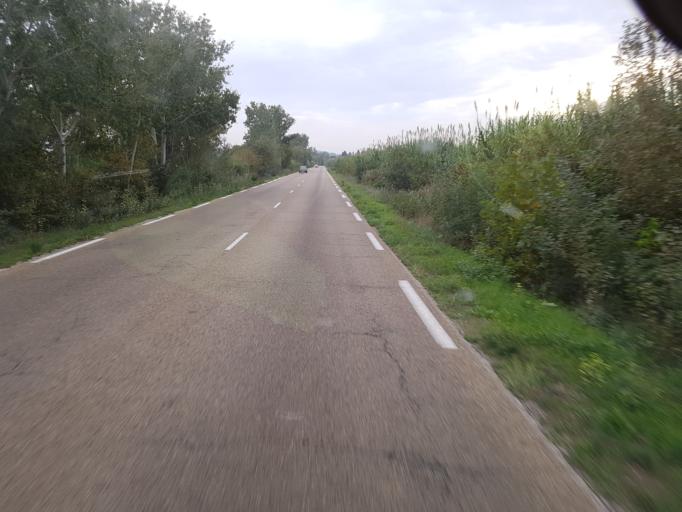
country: FR
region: Provence-Alpes-Cote d'Azur
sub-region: Departement des Bouches-du-Rhone
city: Barbentane
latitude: 43.9168
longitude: 4.7277
